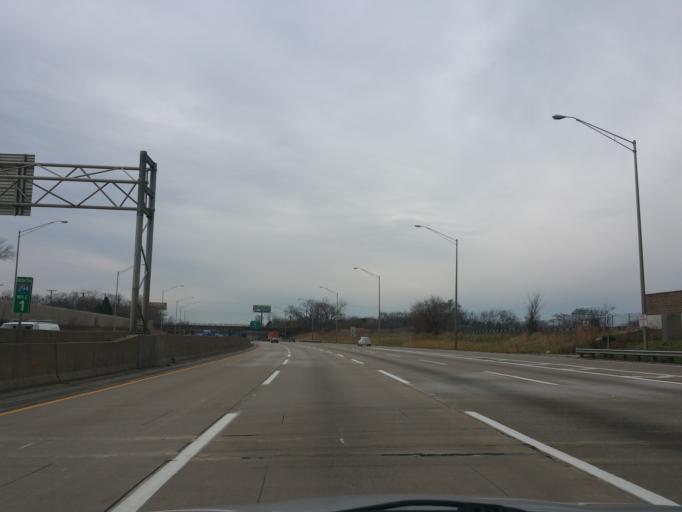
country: US
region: Illinois
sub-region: Cook County
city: Thornton
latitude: 41.5793
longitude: -87.6031
